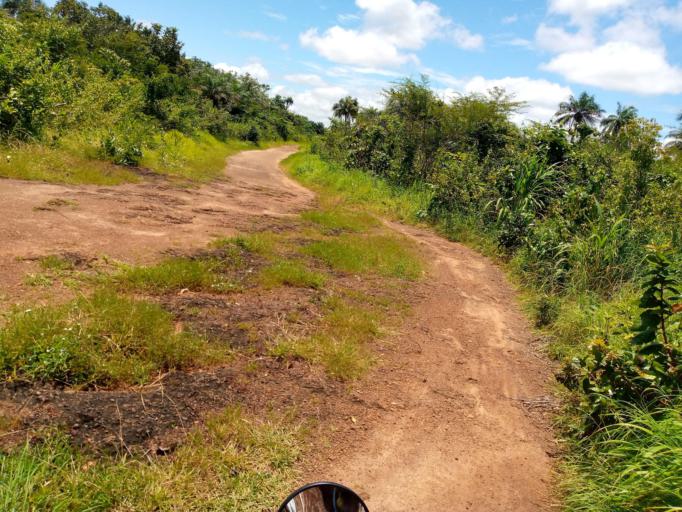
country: SL
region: Northern Province
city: Binkolo
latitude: 9.0647
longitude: -12.1495
